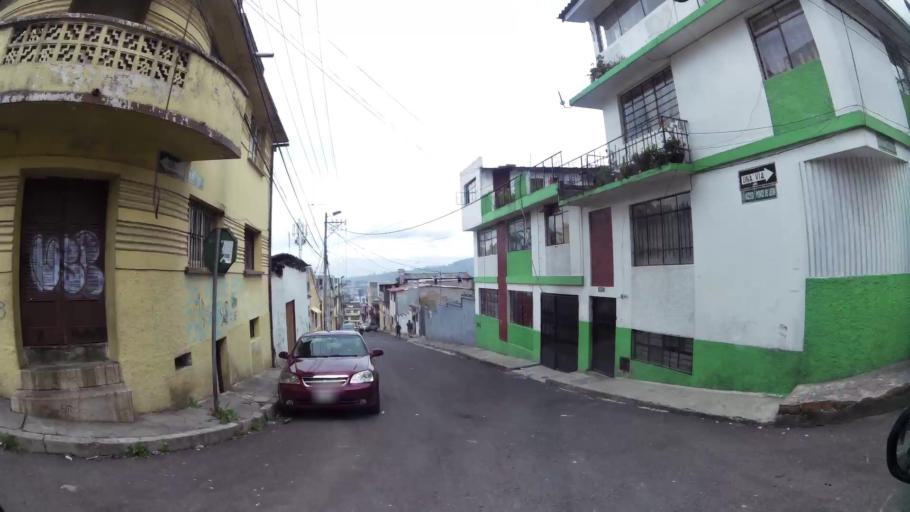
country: EC
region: Pichincha
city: Quito
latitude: -0.1917
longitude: -78.5084
